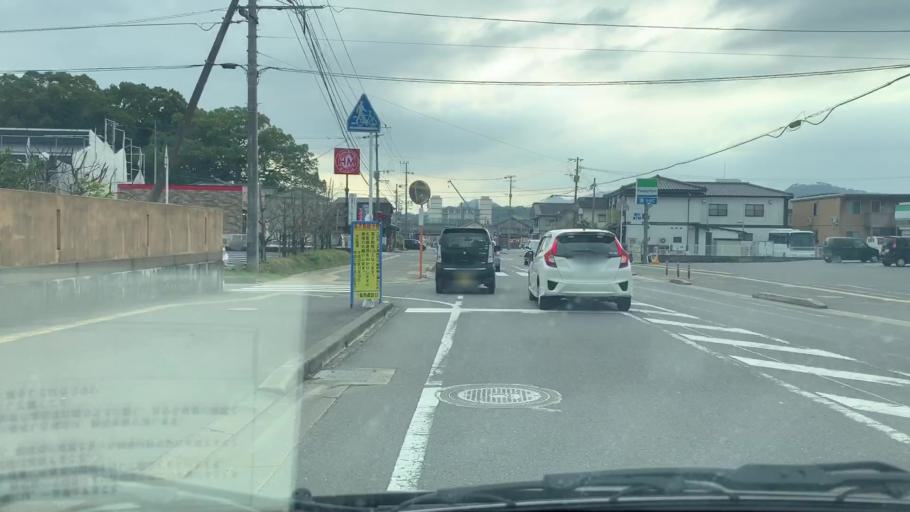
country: JP
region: Saga Prefecture
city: Takeocho-takeo
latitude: 33.2002
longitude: 130.0245
